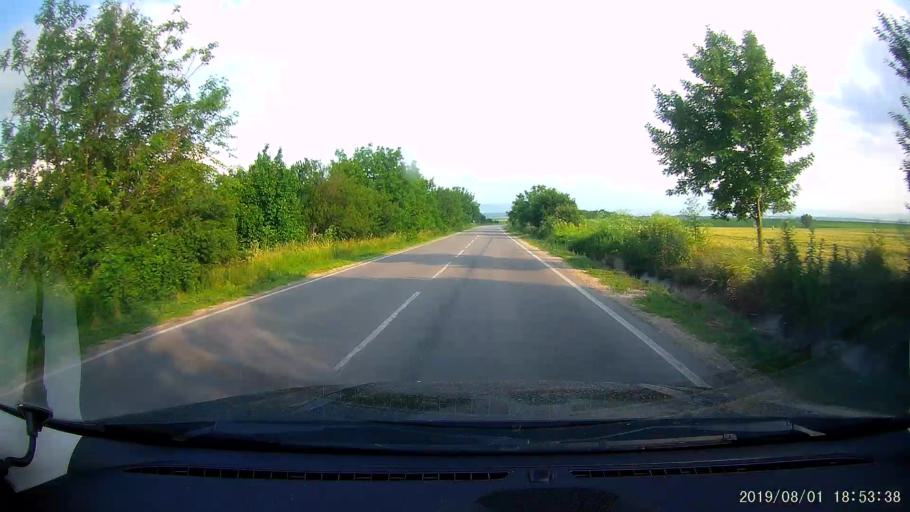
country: BG
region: Shumen
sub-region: Obshtina Shumen
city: Shumen
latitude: 43.2177
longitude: 26.9960
